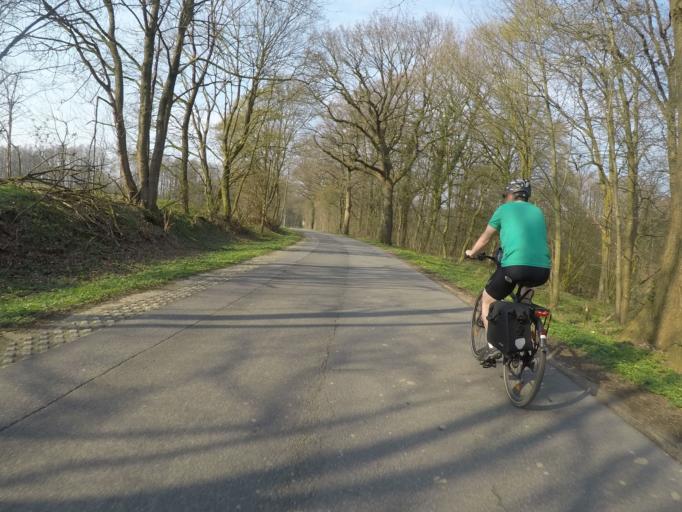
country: DE
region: Schleswig-Holstein
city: Kukels
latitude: 53.8881
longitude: 10.2404
